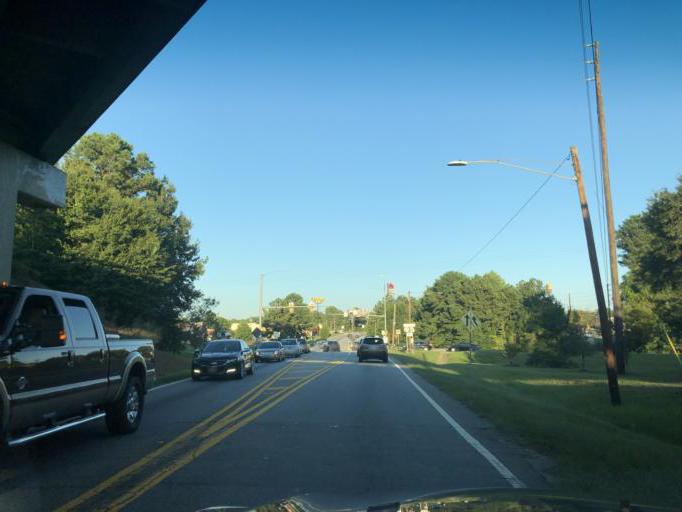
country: US
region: Georgia
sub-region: Muscogee County
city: Columbus
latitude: 32.5224
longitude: -84.8922
